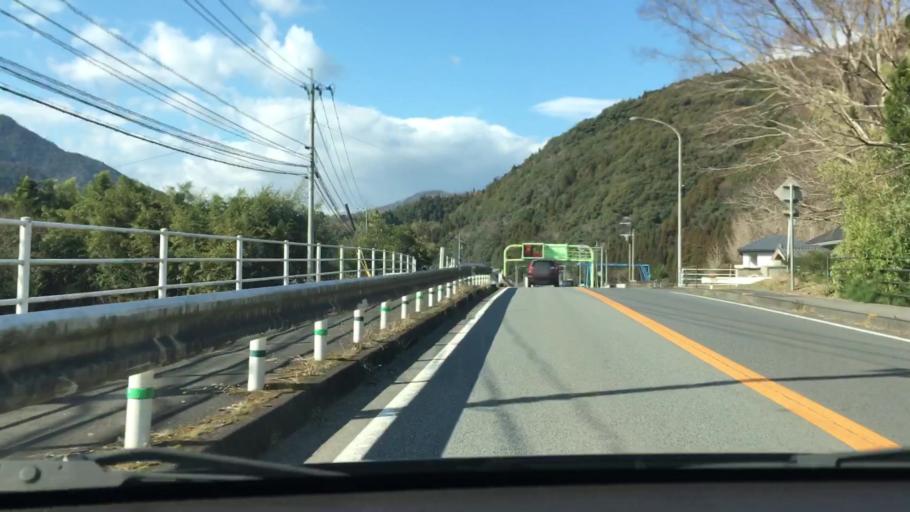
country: JP
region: Oita
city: Saiki
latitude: 32.9867
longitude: 131.8390
